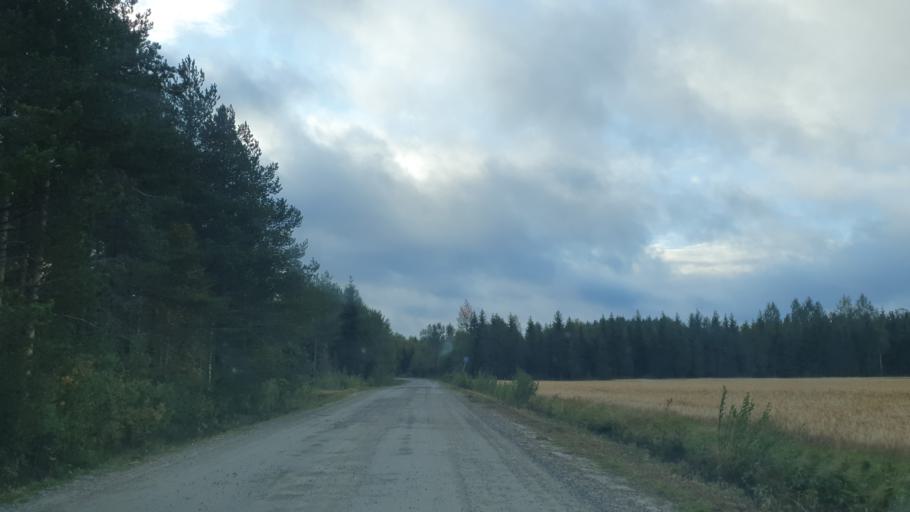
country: FI
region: Kainuu
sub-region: Kehys-Kainuu
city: Kuhmo
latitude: 64.1332
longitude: 29.5827
